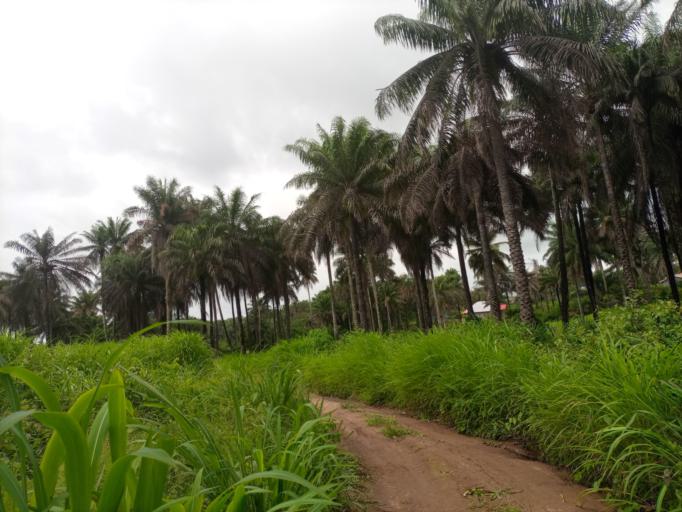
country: SL
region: Northern Province
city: Sawkta
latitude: 8.6459
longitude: -13.1899
